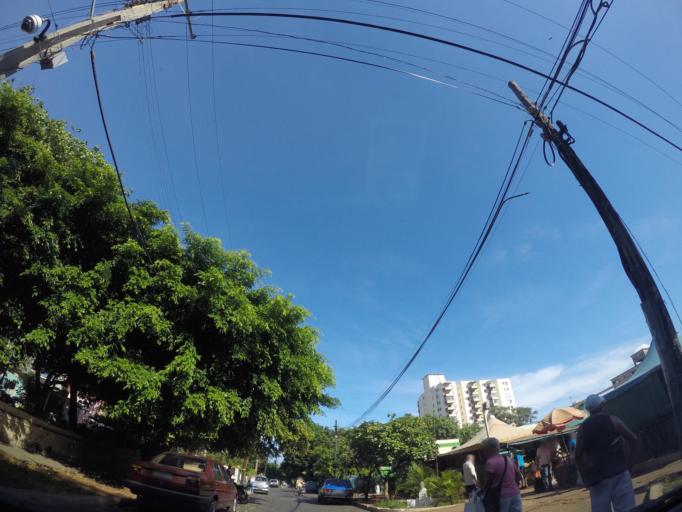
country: CU
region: La Habana
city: Havana
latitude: 23.1417
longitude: -82.3866
